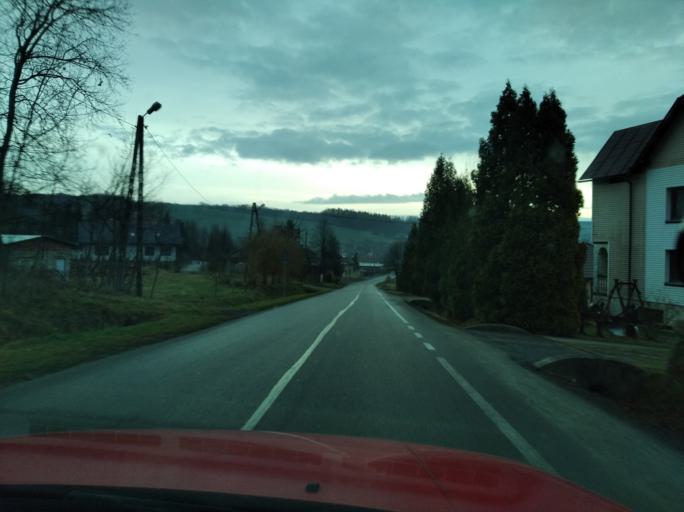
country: PL
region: Subcarpathian Voivodeship
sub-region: Powiat strzyzowski
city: Niebylec
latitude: 49.8580
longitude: 21.9001
